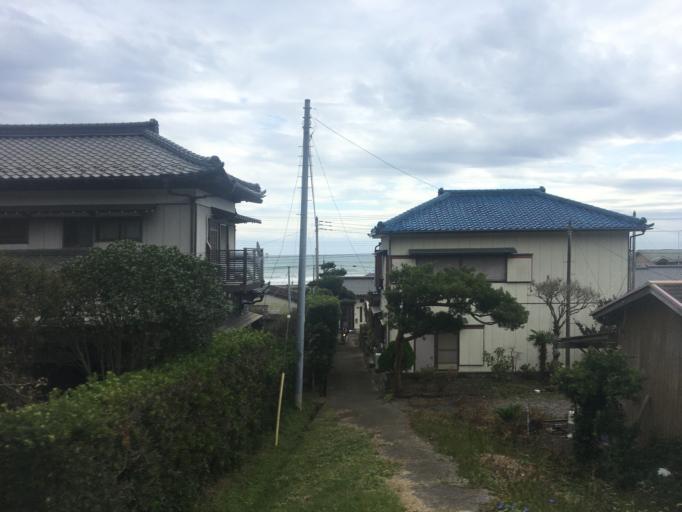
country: JP
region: Chiba
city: Kawaguchi
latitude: 35.0307
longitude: 139.9992
